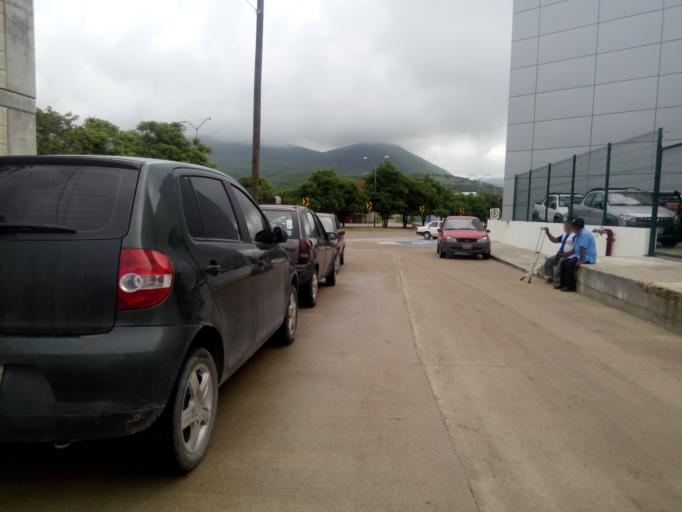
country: MX
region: Chiapas
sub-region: San Fernando
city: Alvaro Obregon
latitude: 16.7702
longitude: -93.1936
